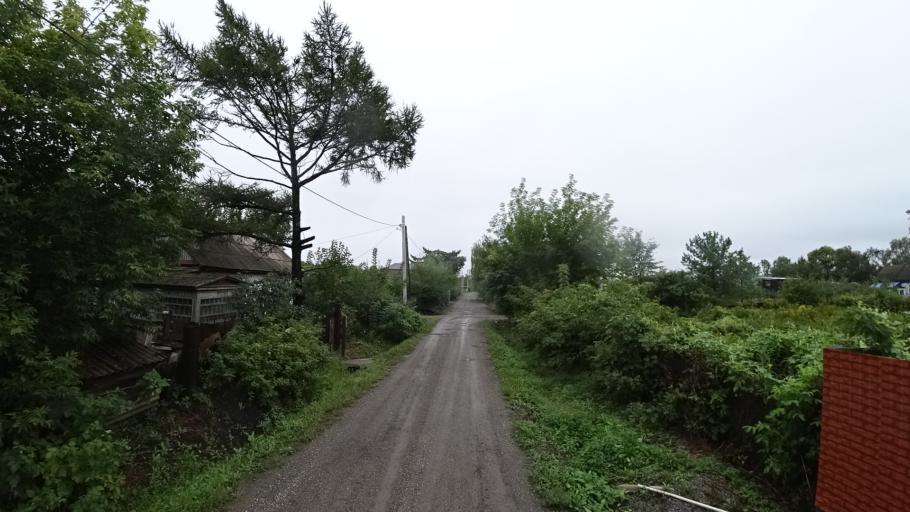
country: RU
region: Primorskiy
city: Monastyrishche
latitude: 44.2044
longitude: 132.4235
